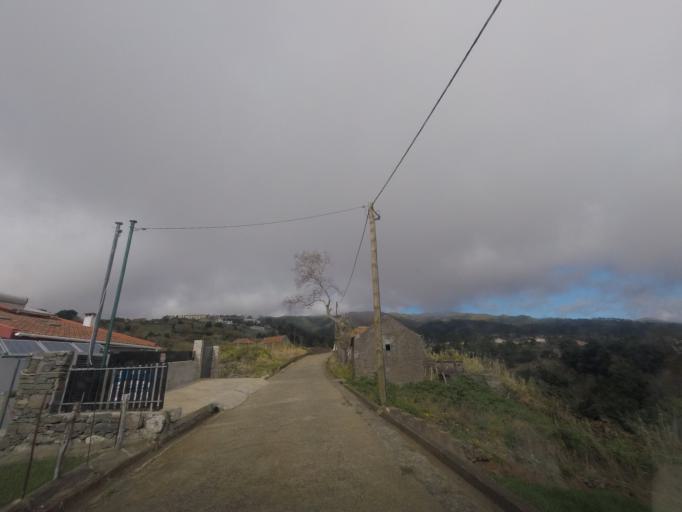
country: PT
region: Madeira
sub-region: Calheta
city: Faja da Ovelha
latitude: 32.7619
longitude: -17.2175
